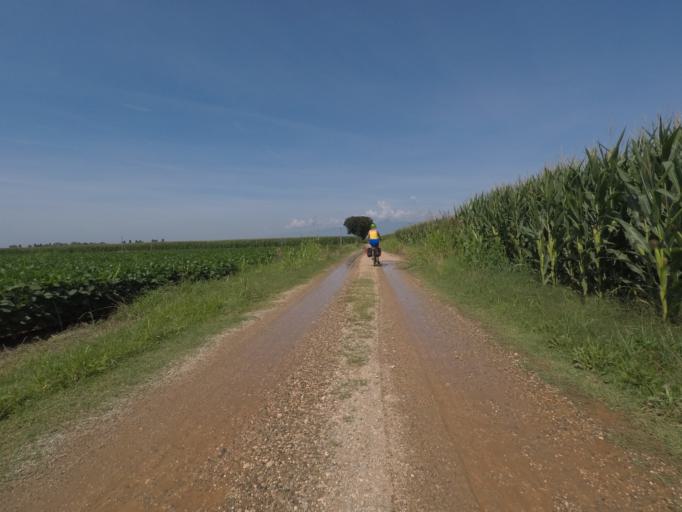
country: IT
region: Friuli Venezia Giulia
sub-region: Provincia di Udine
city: Flaibano
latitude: 46.0825
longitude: 12.9695
